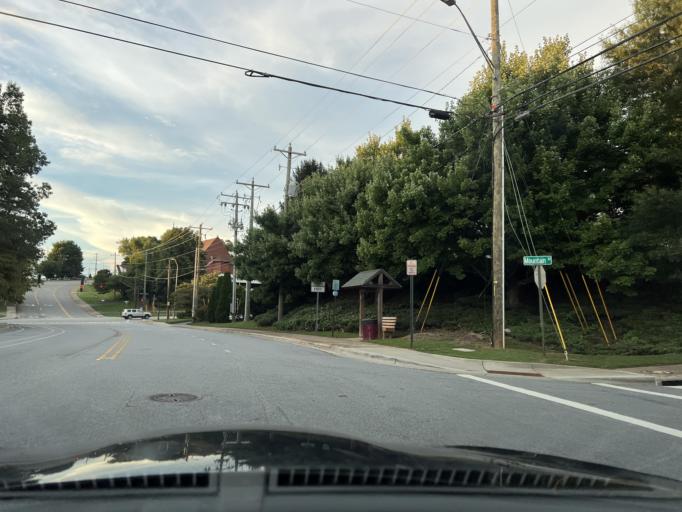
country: US
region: North Carolina
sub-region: Buncombe County
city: Asheville
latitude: 35.5973
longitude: -82.5439
